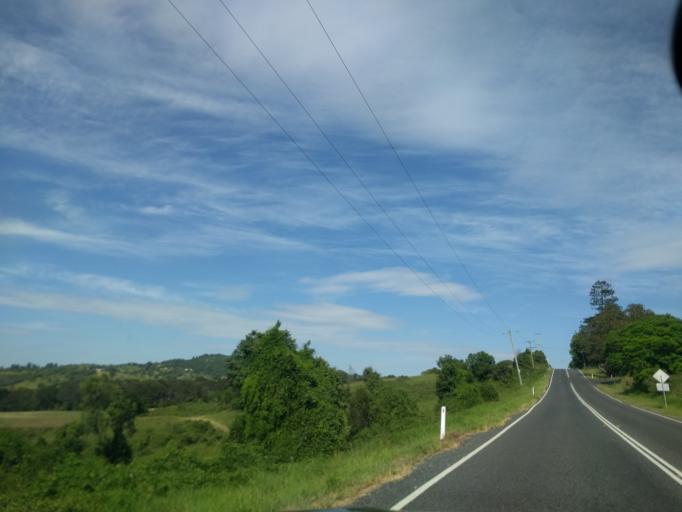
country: AU
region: Queensland
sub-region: Ipswich
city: Thagoona
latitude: -27.5949
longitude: 152.5667
